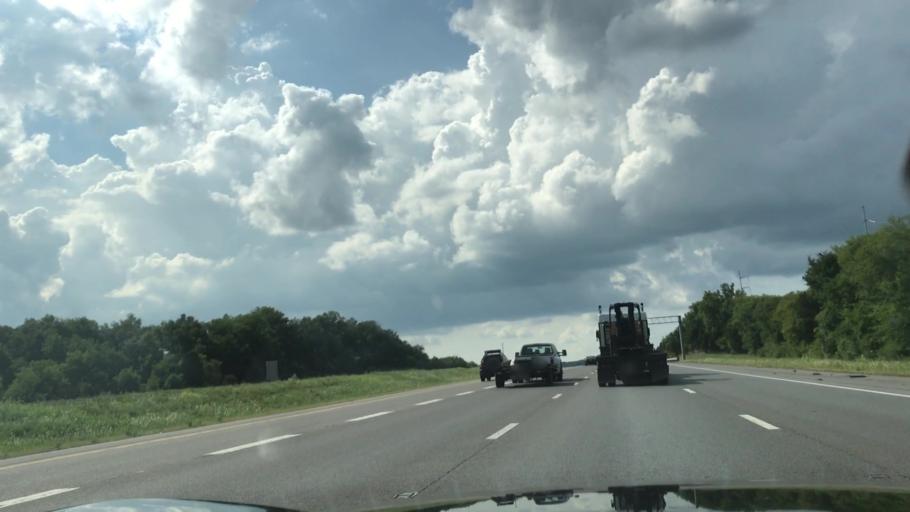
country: US
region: Tennessee
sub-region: Rutherford County
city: Smyrna
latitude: 35.9578
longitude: -86.5572
